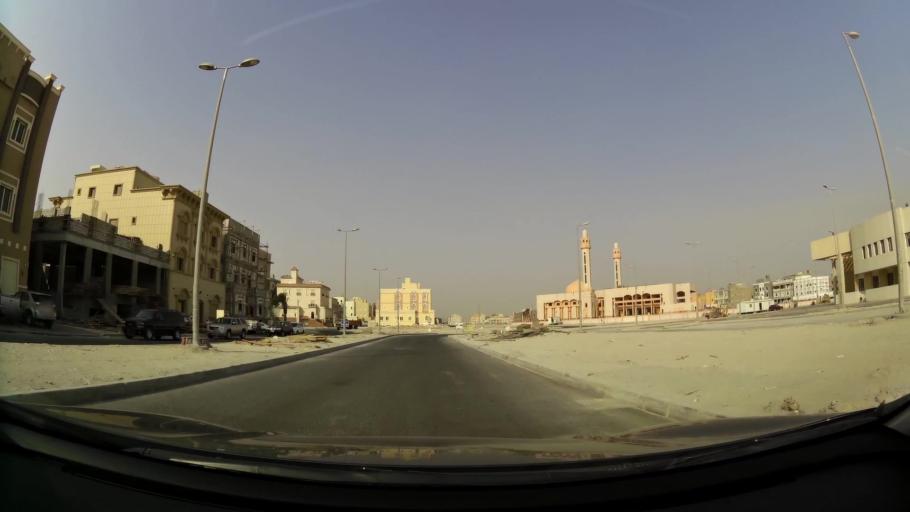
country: KW
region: Al Asimah
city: Ar Rabiyah
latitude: 29.3275
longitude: 47.8121
